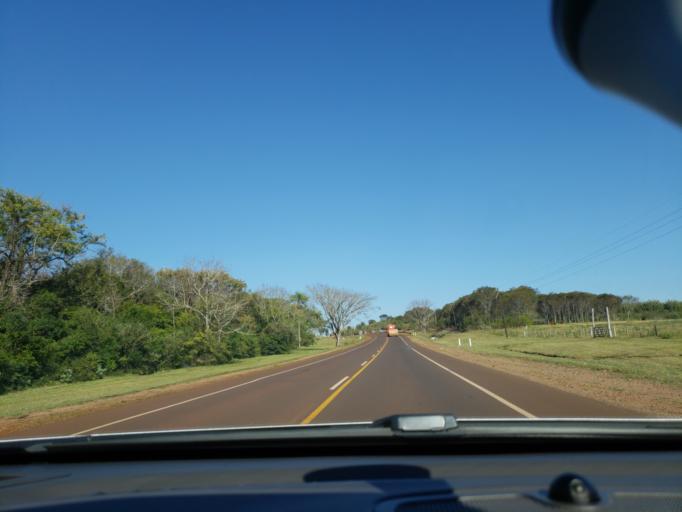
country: AR
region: Misiones
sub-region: Departamento de Apostoles
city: San Jose
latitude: -27.7946
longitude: -55.7712
